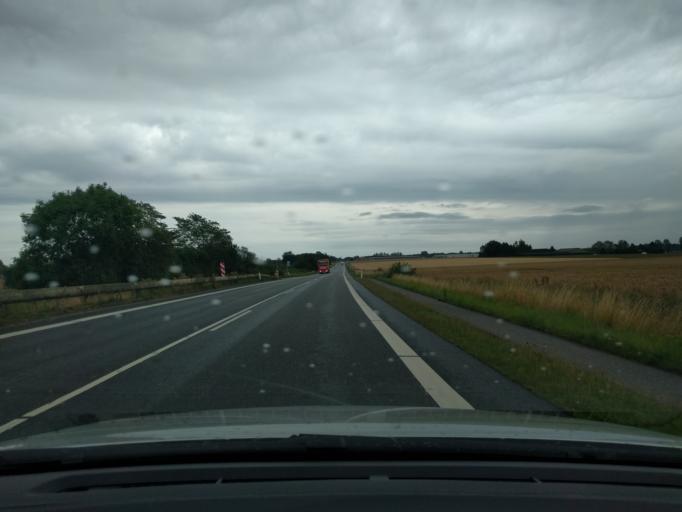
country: DK
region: South Denmark
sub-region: Kerteminde Kommune
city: Langeskov
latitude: 55.3815
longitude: 10.5418
